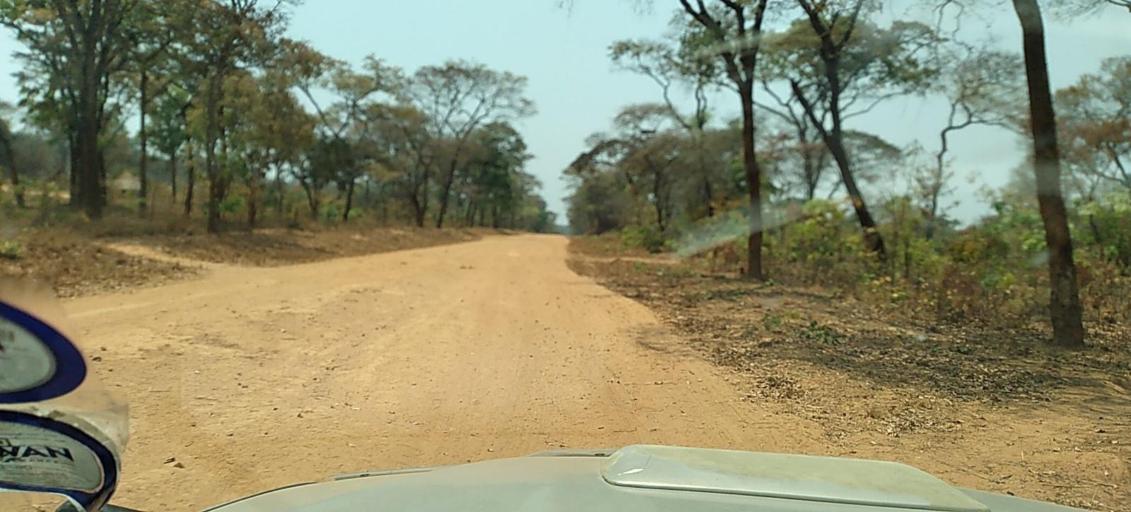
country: ZM
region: North-Western
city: Kasempa
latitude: -13.5481
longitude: 26.0333
